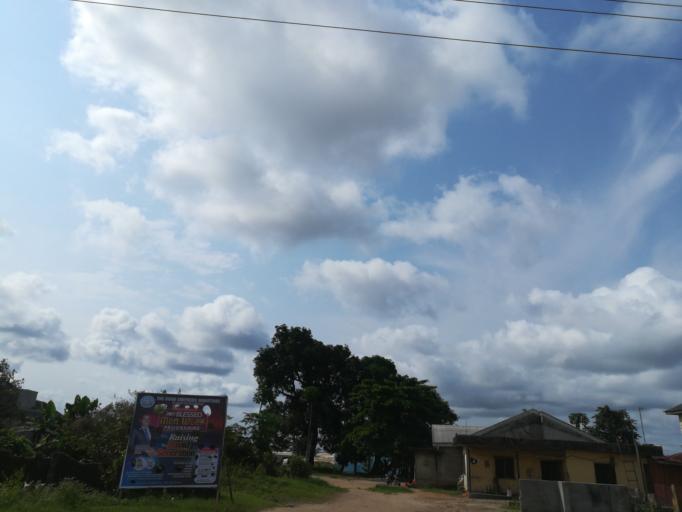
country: NG
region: Rivers
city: Okrika
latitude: 4.7610
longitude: 7.0900
